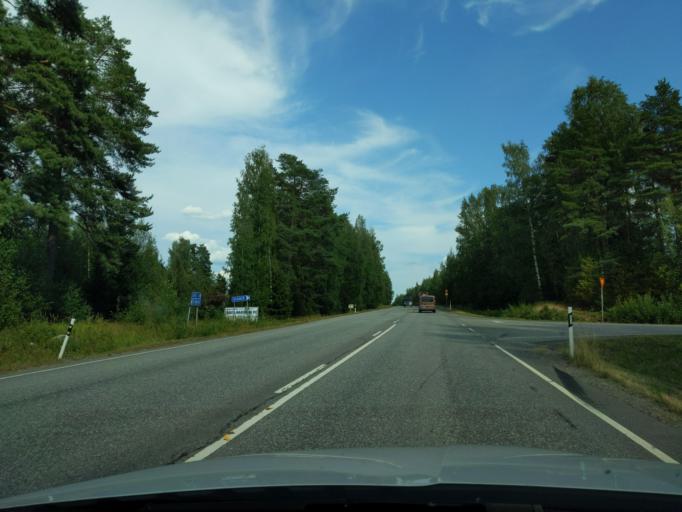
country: FI
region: Haeme
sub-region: Haemeenlinna
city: Hauho
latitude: 61.1744
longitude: 24.5801
